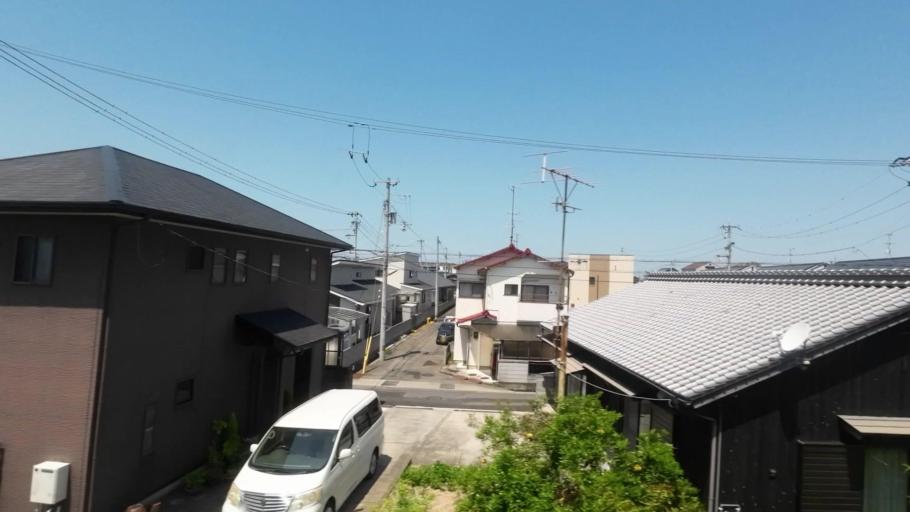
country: JP
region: Ehime
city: Hojo
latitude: 33.9790
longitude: 132.7783
